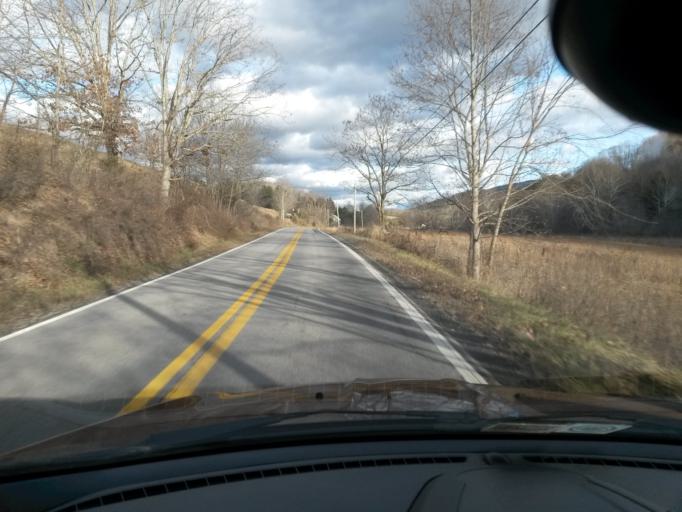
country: US
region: West Virginia
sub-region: Monroe County
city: Union
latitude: 37.4775
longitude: -80.6420
